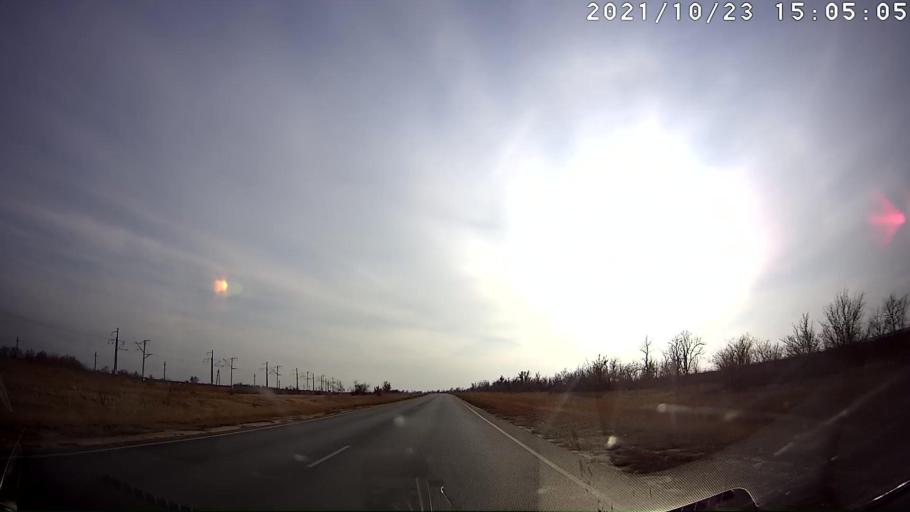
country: RU
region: Volgograd
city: Volgograd
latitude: 48.3896
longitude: 44.3621
